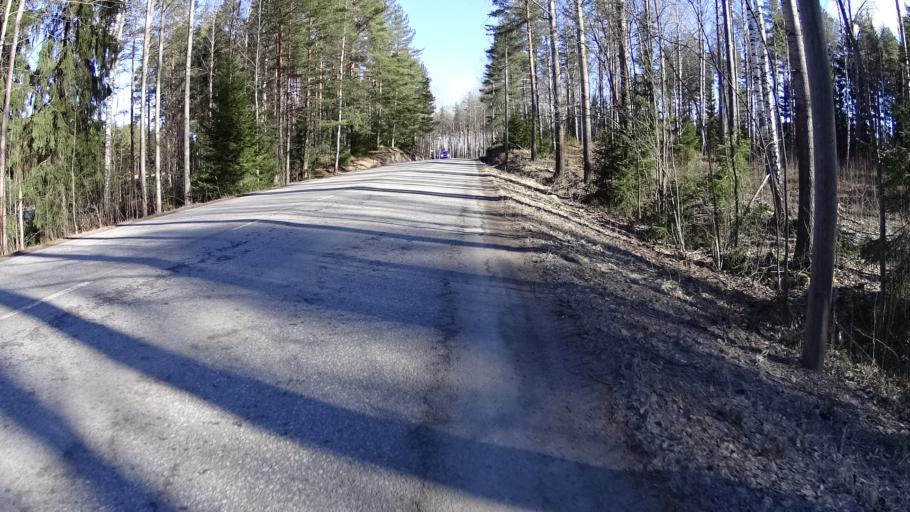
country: FI
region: Uusimaa
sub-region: Helsinki
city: Kauniainen
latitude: 60.2666
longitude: 24.7073
